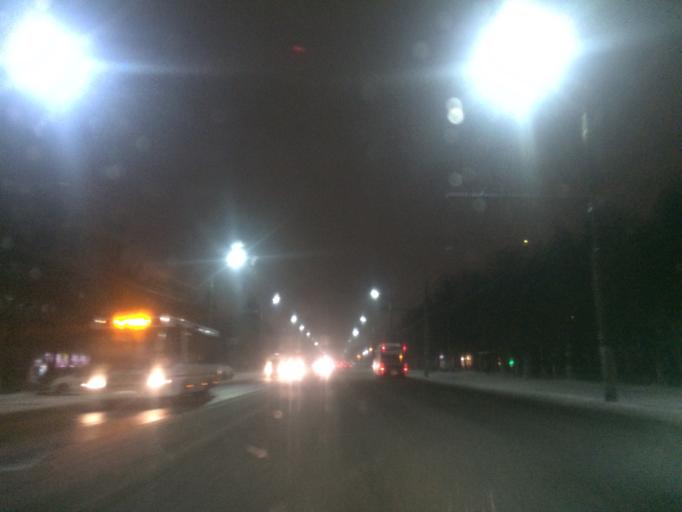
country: RU
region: Tula
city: Mendeleyevskiy
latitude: 54.1596
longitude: 37.5859
